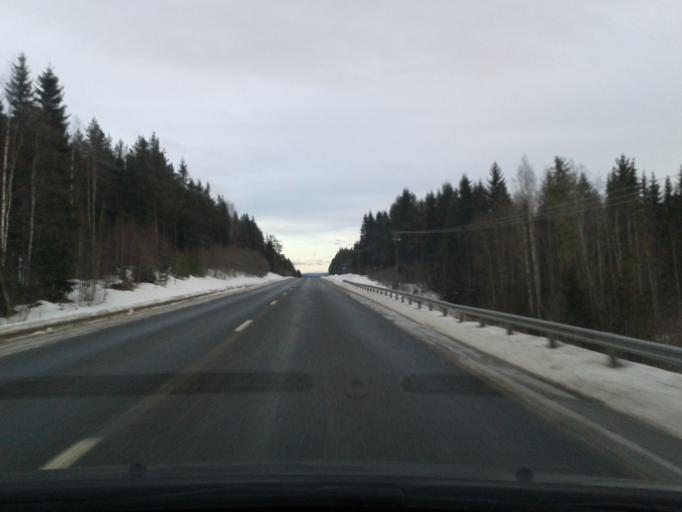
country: SE
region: Vaesternorrland
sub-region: Solleftea Kommun
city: Solleftea
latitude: 63.3594
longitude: 17.0245
